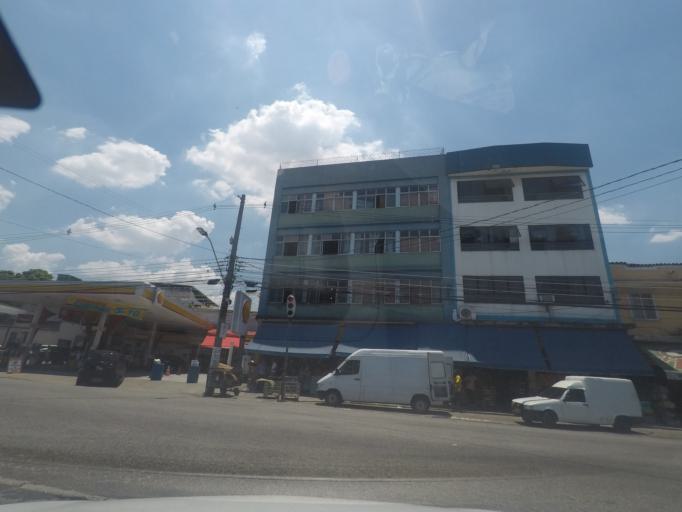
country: BR
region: Rio de Janeiro
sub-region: Duque De Caxias
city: Duque de Caxias
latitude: -22.7834
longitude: -43.3092
